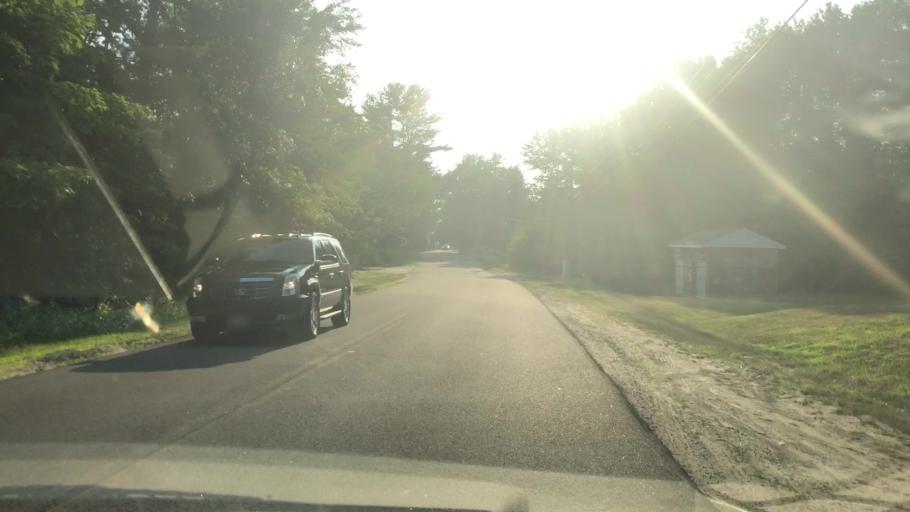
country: US
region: New Hampshire
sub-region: Hillsborough County
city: Milford
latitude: 42.8157
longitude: -71.6343
